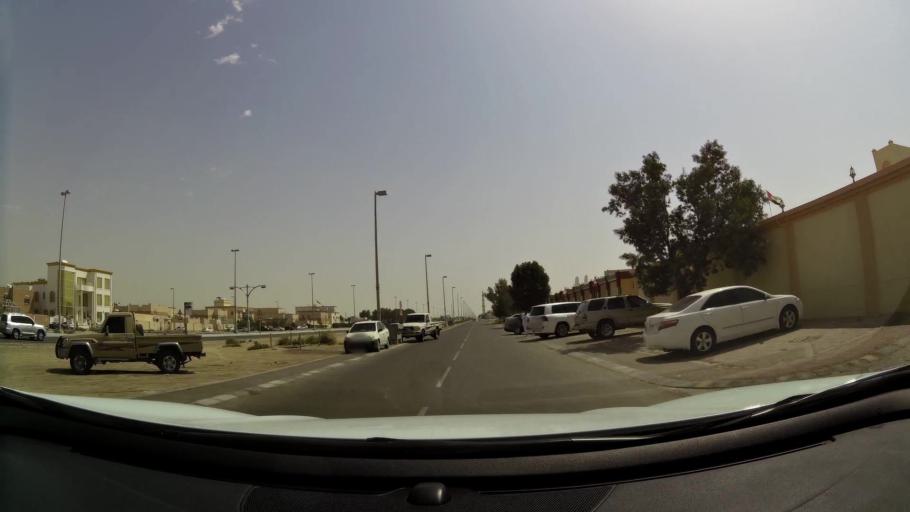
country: AE
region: Abu Dhabi
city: Abu Dhabi
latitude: 24.3051
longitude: 54.6407
